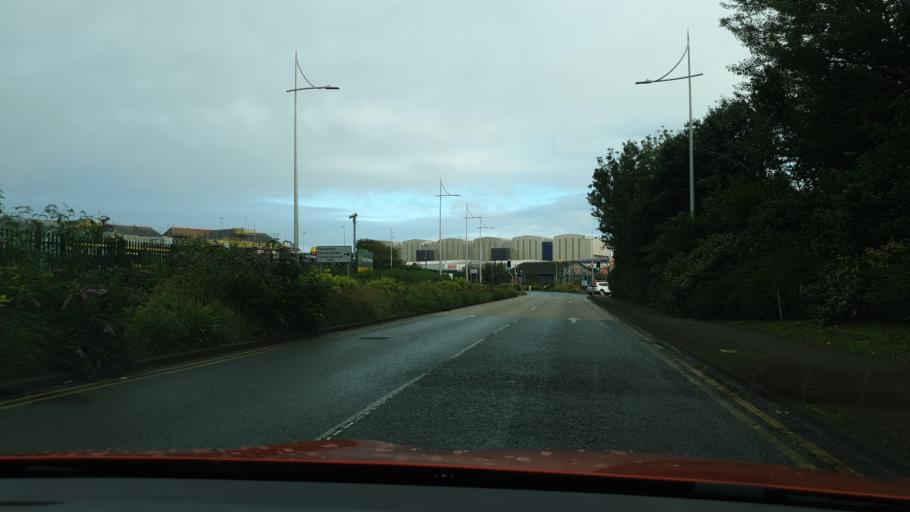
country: GB
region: England
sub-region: Cumbria
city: Barrow in Furness
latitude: 54.1173
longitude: -3.2384
